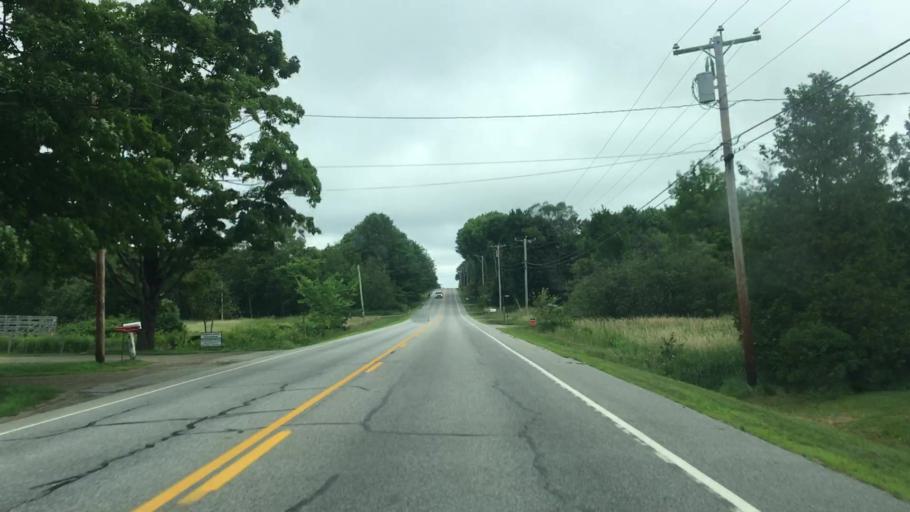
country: US
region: Maine
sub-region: Sagadahoc County
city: Richmond
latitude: 44.1404
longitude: -69.7419
